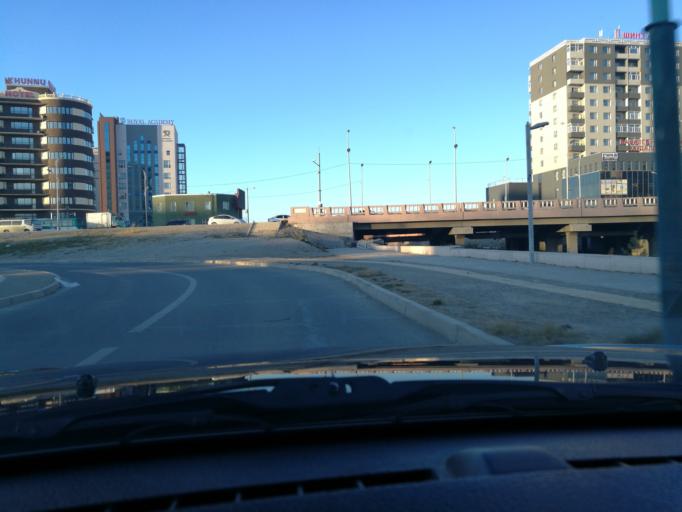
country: MN
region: Ulaanbaatar
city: Ulaanbaatar
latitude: 47.9288
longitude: 106.9311
